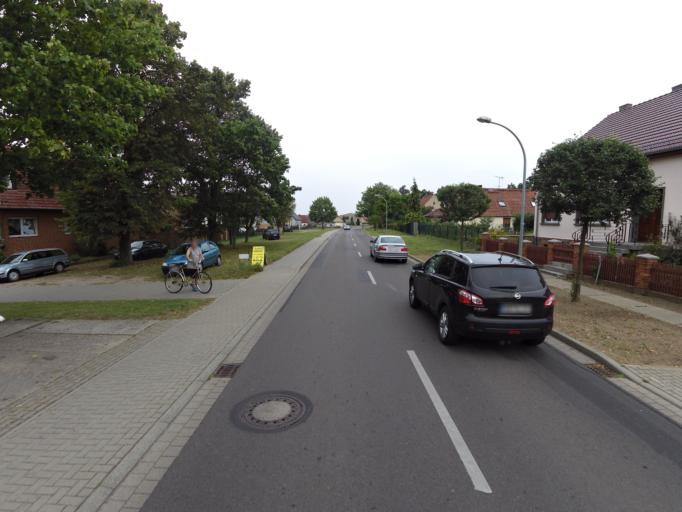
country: DE
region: Brandenburg
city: Zehdenick
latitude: 53.0119
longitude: 13.2857
